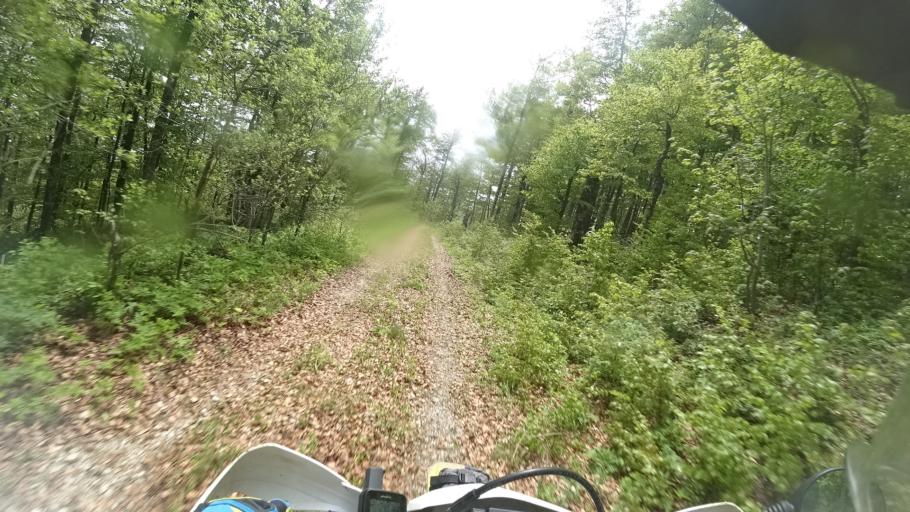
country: BA
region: Federation of Bosnia and Herzegovina
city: Orasac
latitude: 44.5694
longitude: 15.8771
